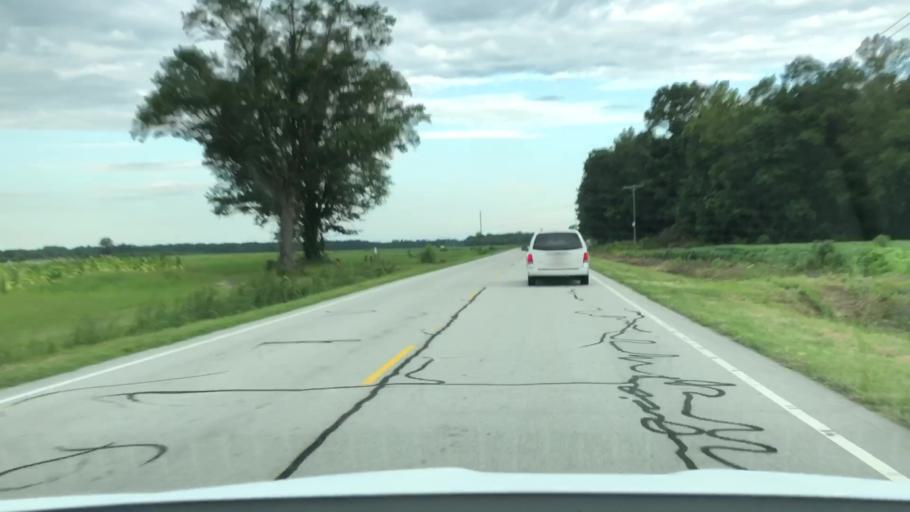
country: US
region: North Carolina
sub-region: Jones County
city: Trenton
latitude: 35.0790
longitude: -77.4273
